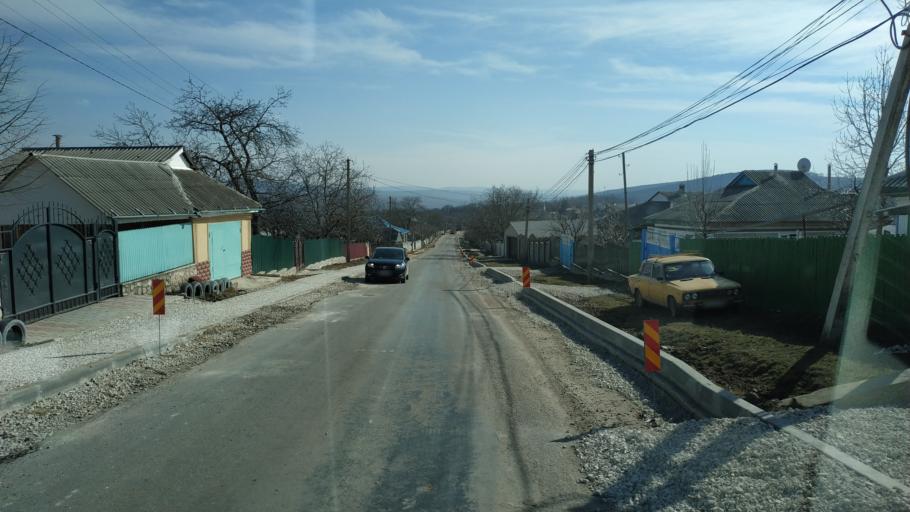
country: MD
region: Nisporeni
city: Nisporeni
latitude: 47.1995
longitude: 28.0621
